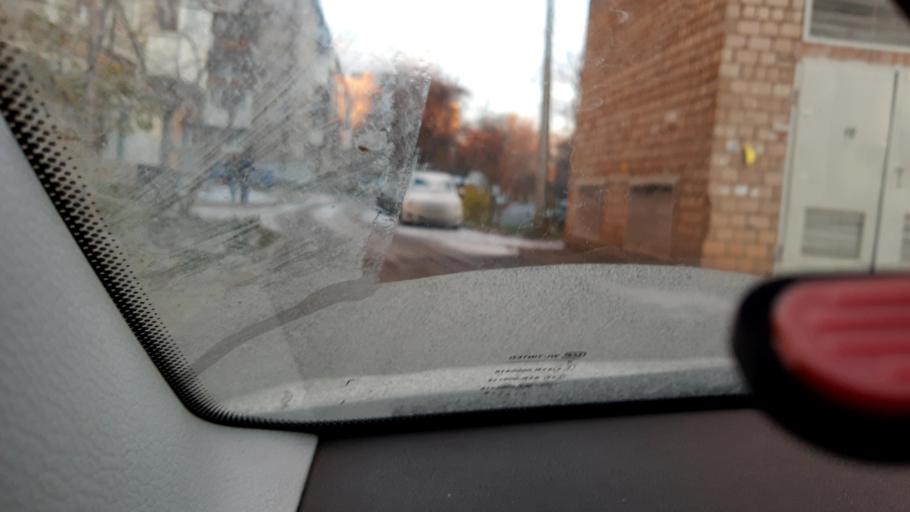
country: RU
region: Bashkortostan
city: Ufa
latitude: 54.8094
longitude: 56.1221
